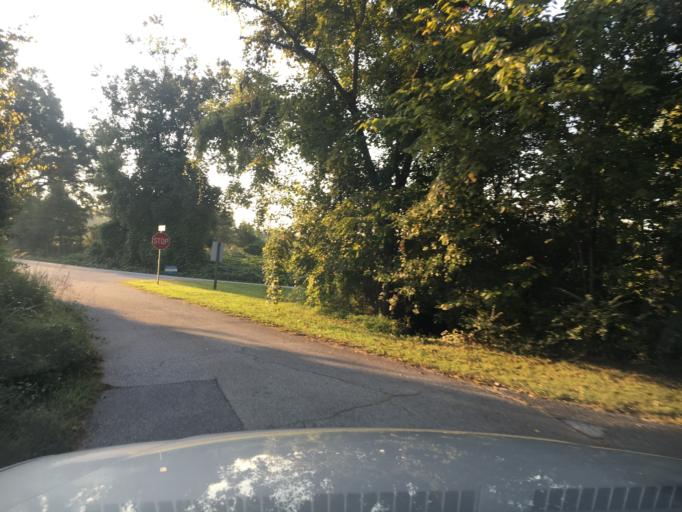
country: US
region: South Carolina
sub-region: Spartanburg County
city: Duncan
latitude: 34.8596
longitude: -82.1169
